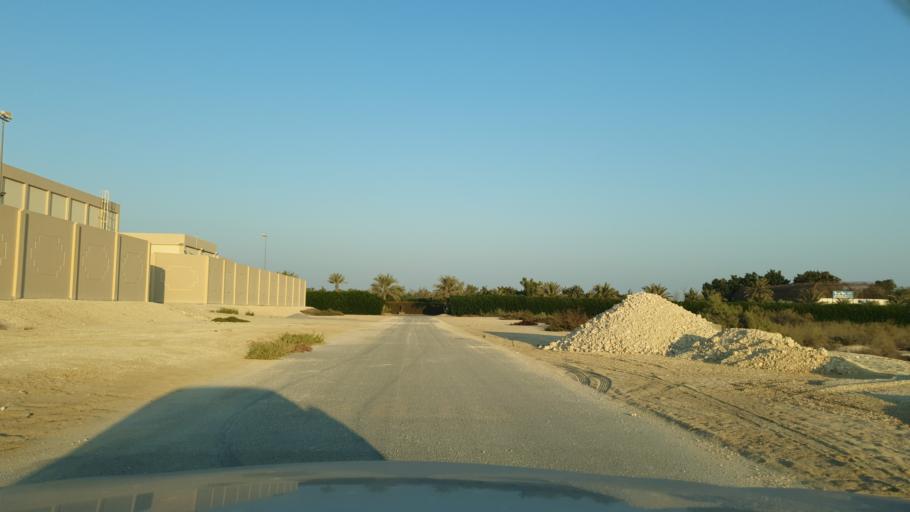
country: BH
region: Central Governorate
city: Dar Kulayb
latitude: 26.0171
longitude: 50.4928
